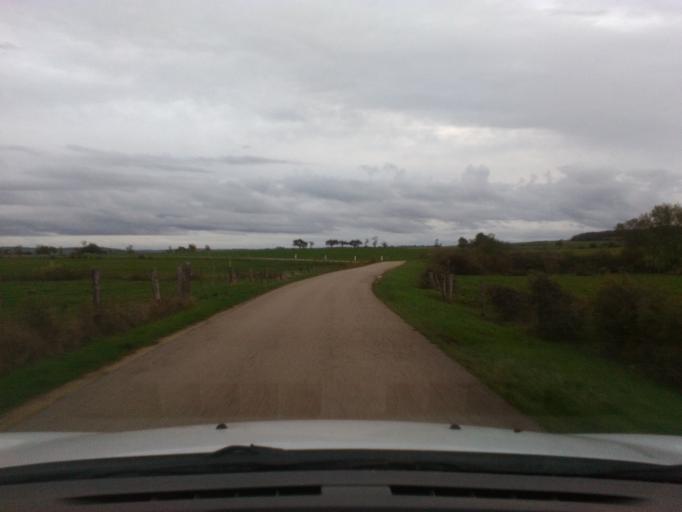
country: FR
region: Lorraine
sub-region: Departement des Vosges
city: Mirecourt
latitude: 48.3366
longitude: 6.0857
